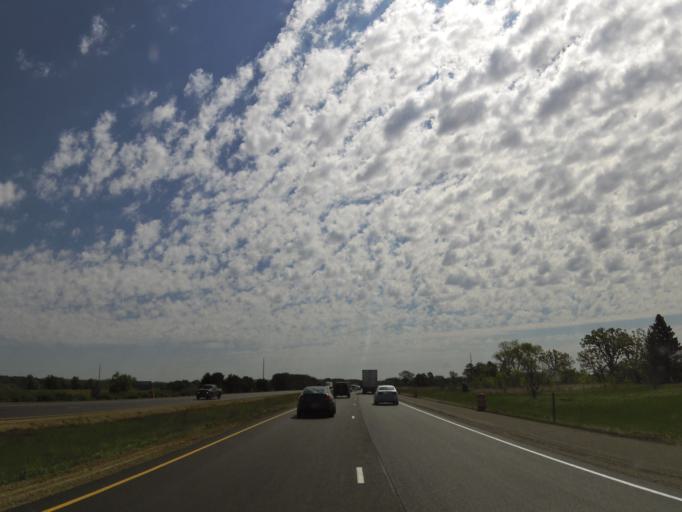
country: US
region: Wisconsin
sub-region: Dunn County
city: Tainter Lake
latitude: 44.9053
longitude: -91.8174
